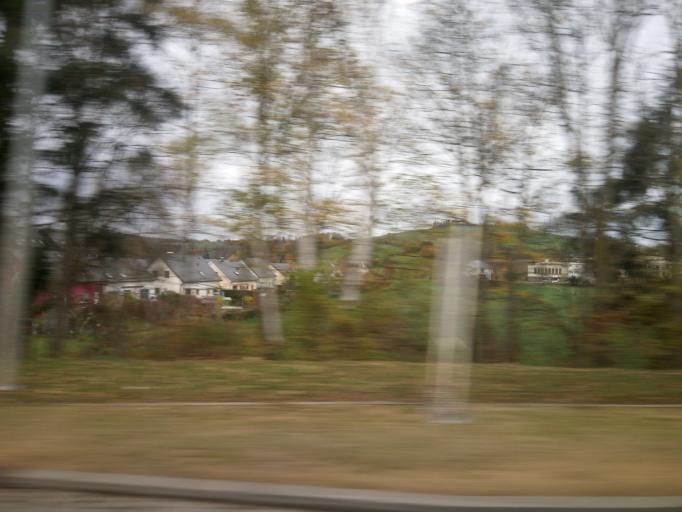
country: LU
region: Diekirch
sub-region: Canton de Diekirch
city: Ettelbruck
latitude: 49.8505
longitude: 6.1154
